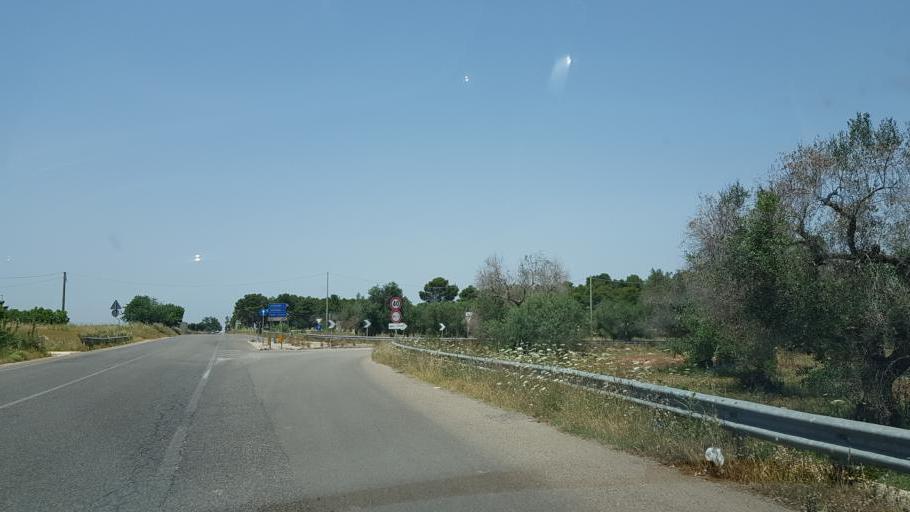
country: IT
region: Apulia
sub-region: Provincia di Lecce
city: Porto Cesareo
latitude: 40.2666
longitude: 17.9127
